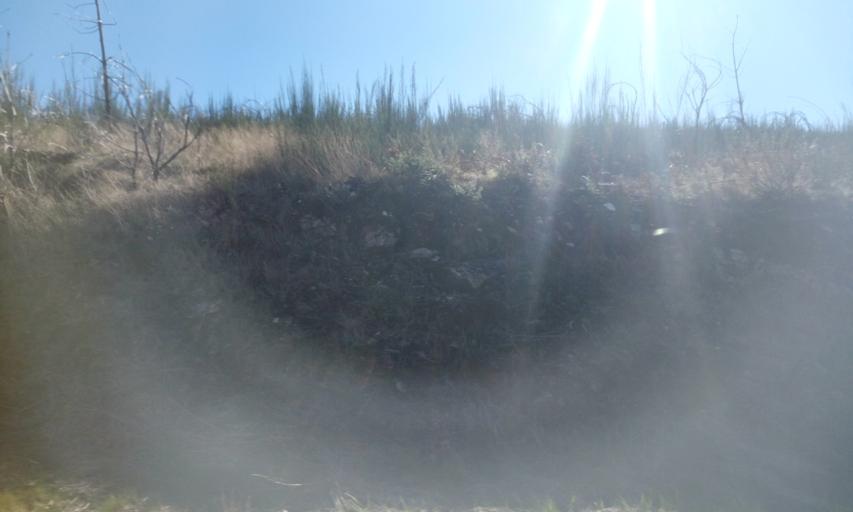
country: PT
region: Guarda
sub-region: Manteigas
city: Manteigas
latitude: 40.4957
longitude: -7.5299
